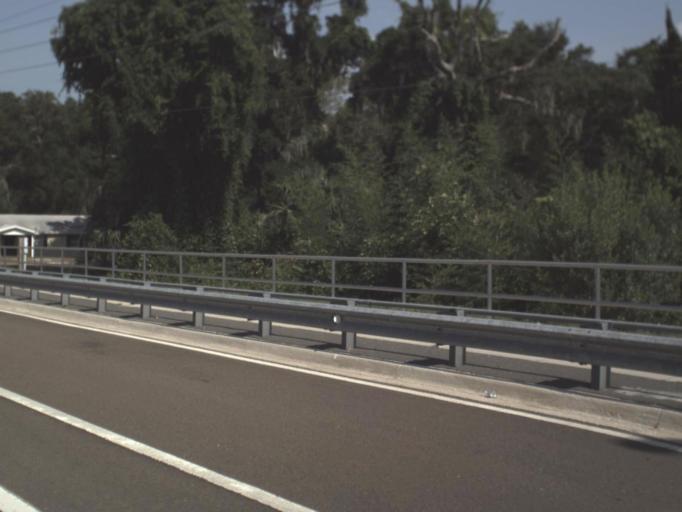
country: US
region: Florida
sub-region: Duval County
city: Atlantic Beach
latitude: 30.3582
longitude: -81.4620
